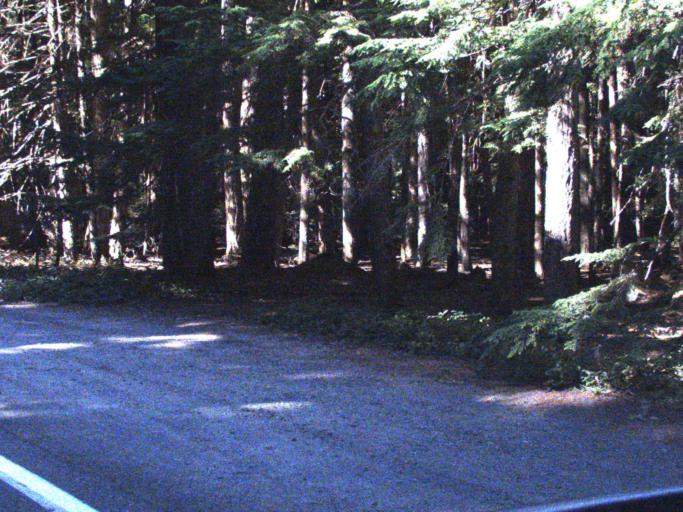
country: US
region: Washington
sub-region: King County
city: Enumclaw
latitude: 46.9780
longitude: -121.5364
